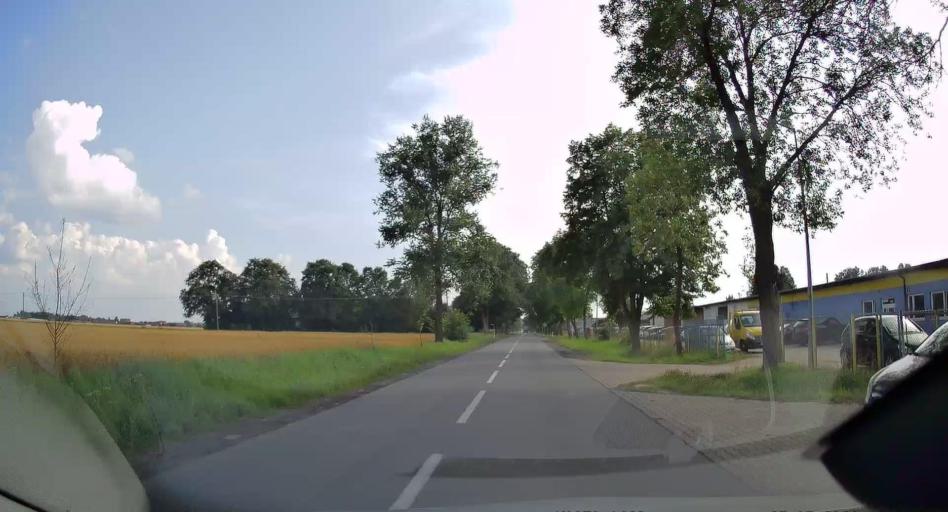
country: PL
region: Lodz Voivodeship
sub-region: Powiat tomaszowski
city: Rzeczyca
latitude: 51.5948
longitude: 20.2915
